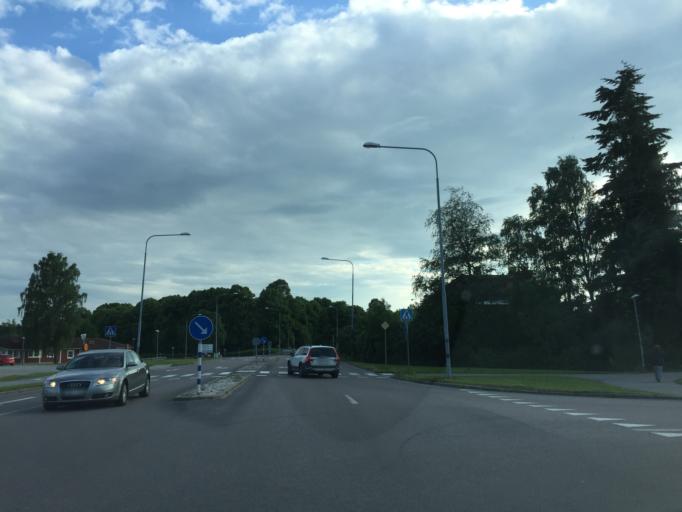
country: SE
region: Vaestmanland
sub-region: Arboga Kommun
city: Arboga
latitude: 59.3945
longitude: 15.8339
